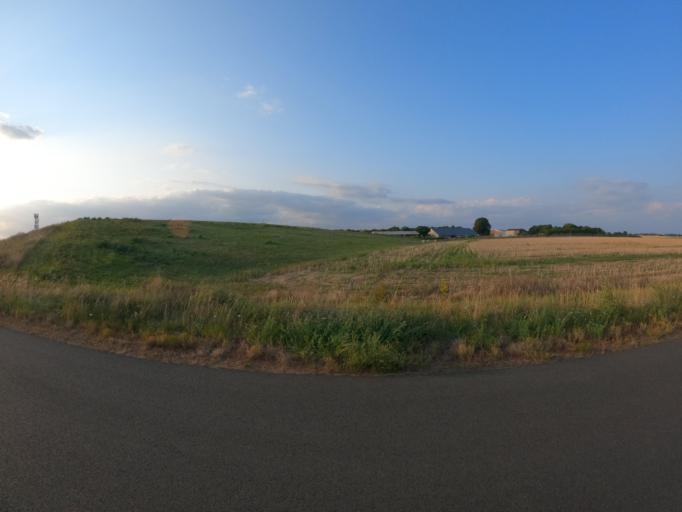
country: FR
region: Pays de la Loire
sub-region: Departement de la Sarthe
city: Brulon
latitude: 47.9083
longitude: -0.2273
